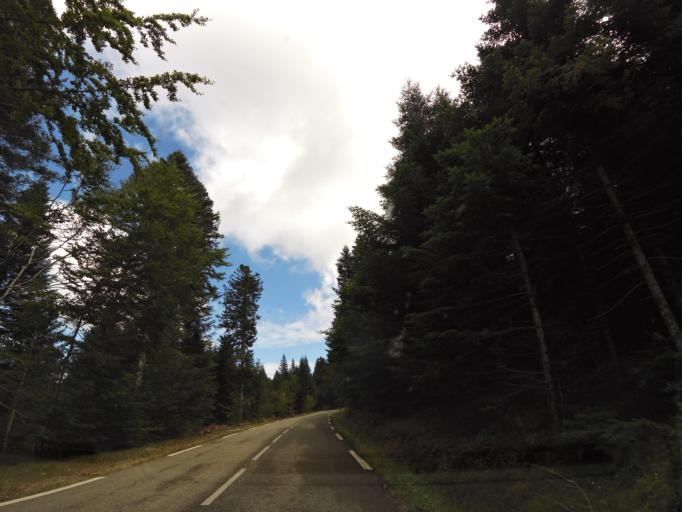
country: FR
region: Languedoc-Roussillon
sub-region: Departement de la Lozere
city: Meyrueis
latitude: 44.1029
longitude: 3.5181
